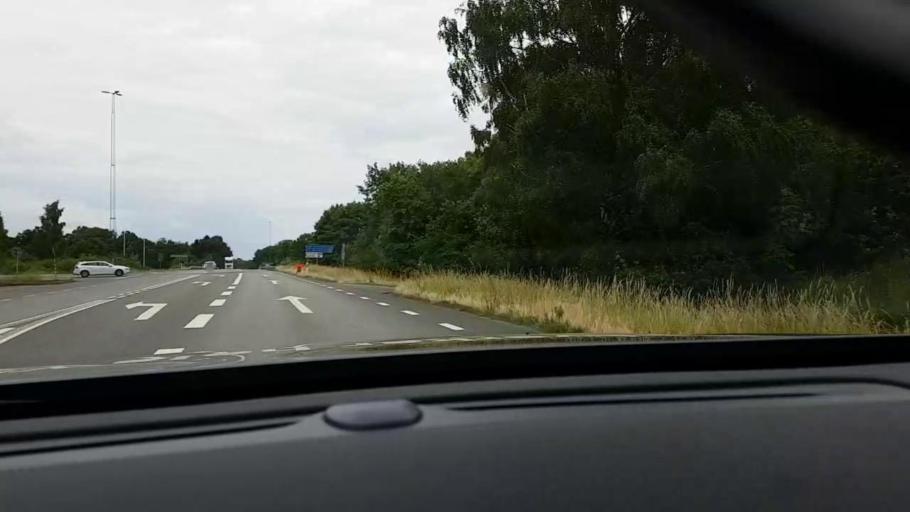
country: SE
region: Skane
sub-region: Hassleholms Kommun
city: Hassleholm
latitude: 56.1384
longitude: 13.8029
